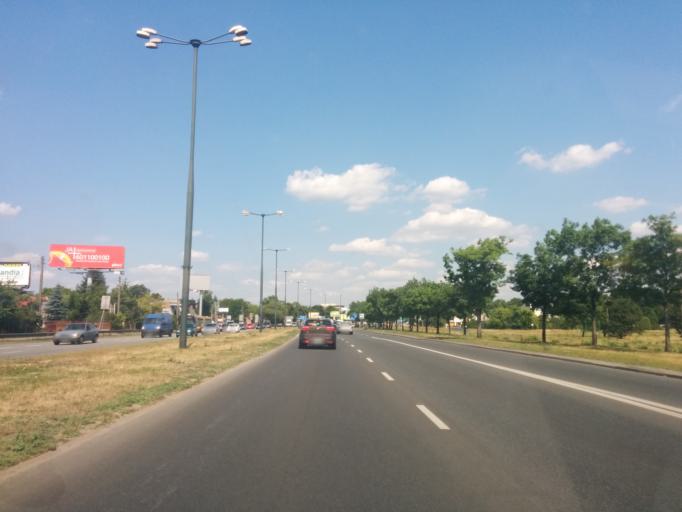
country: PL
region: Masovian Voivodeship
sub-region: Warszawa
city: Bialoleka
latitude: 52.3100
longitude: 20.9809
